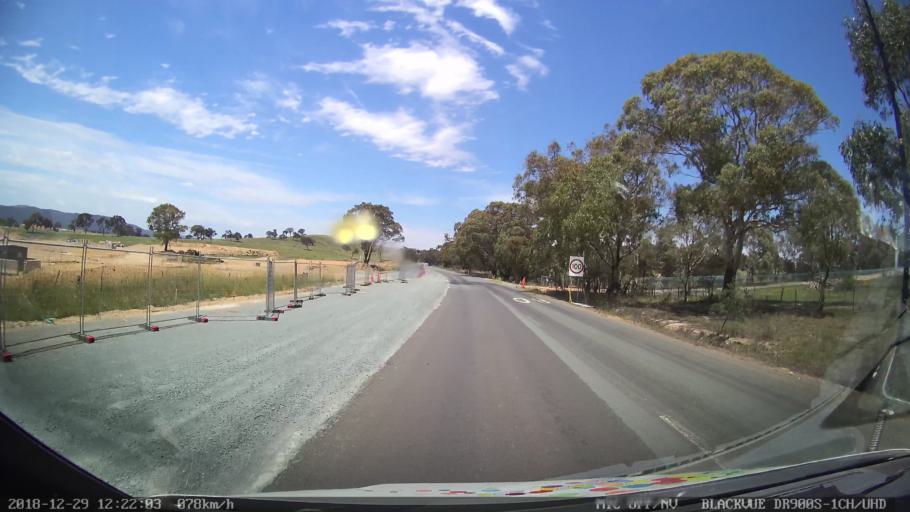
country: AU
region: New South Wales
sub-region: Queanbeyan
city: Queanbeyan
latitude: -35.4198
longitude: 149.2205
